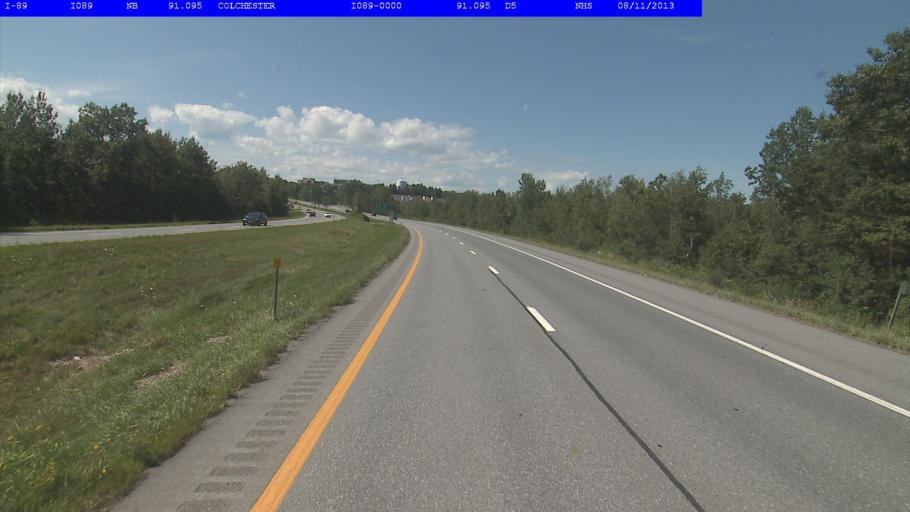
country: US
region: Vermont
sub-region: Chittenden County
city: Winooski
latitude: 44.5021
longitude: -73.1751
